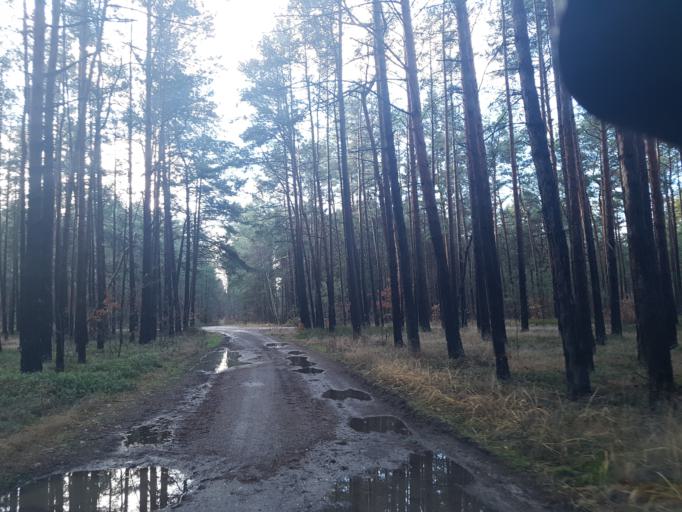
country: DE
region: Brandenburg
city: Ruckersdorf
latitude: 51.5845
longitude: 13.6014
